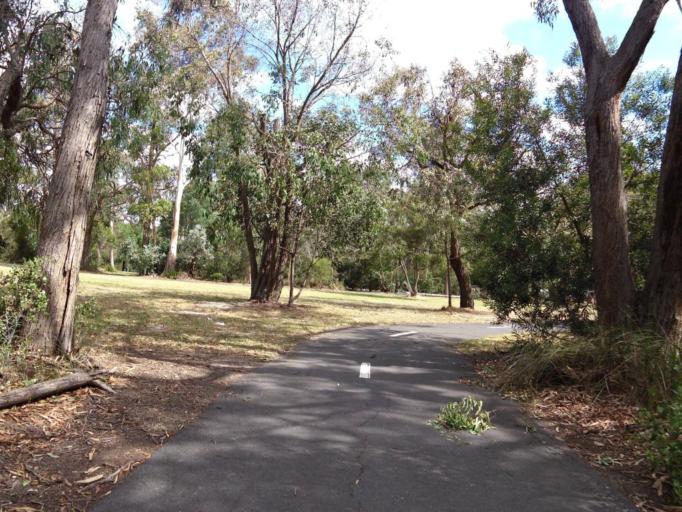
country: AU
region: Victoria
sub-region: Maroondah
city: Ringwood East
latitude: -37.8118
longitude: 145.2368
